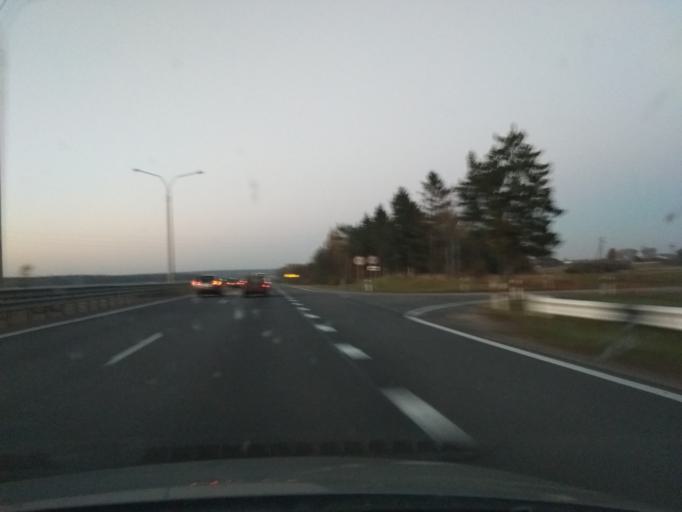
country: BY
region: Minsk
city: Enyerhyetykaw
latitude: 53.6085
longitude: 27.0477
